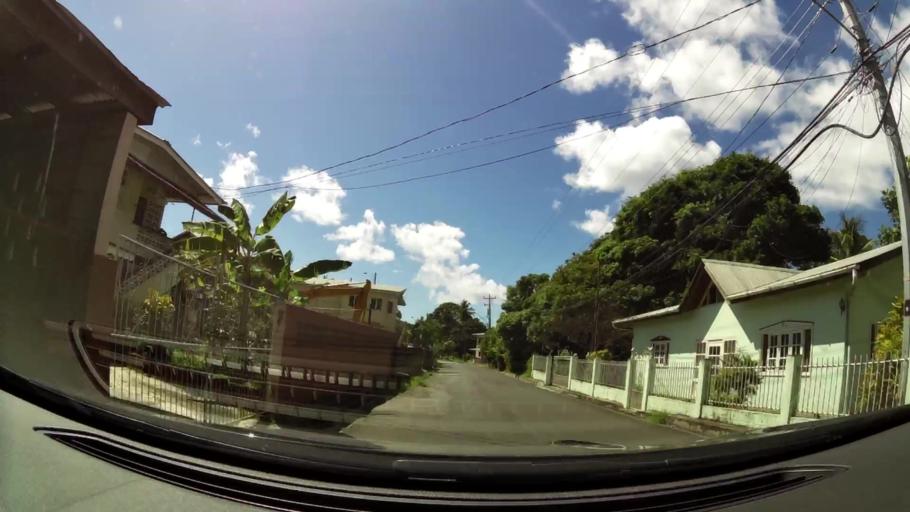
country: TT
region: Tobago
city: Scarborough
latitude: 11.2210
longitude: -60.7716
